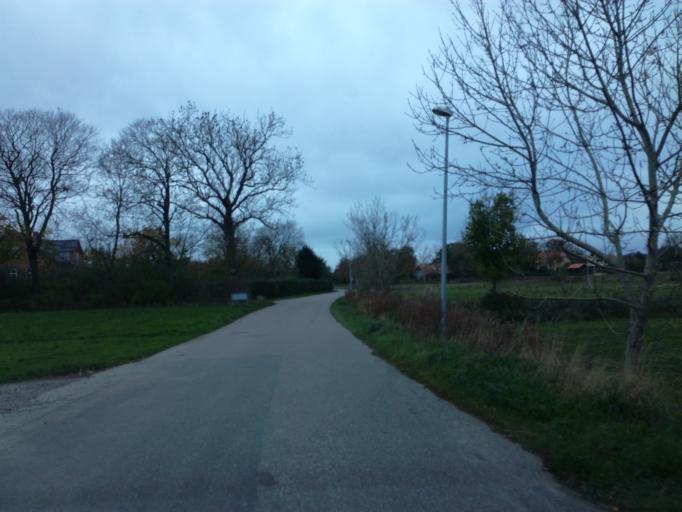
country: DK
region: South Denmark
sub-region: Fredericia Kommune
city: Fredericia
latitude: 55.6216
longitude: 9.7874
